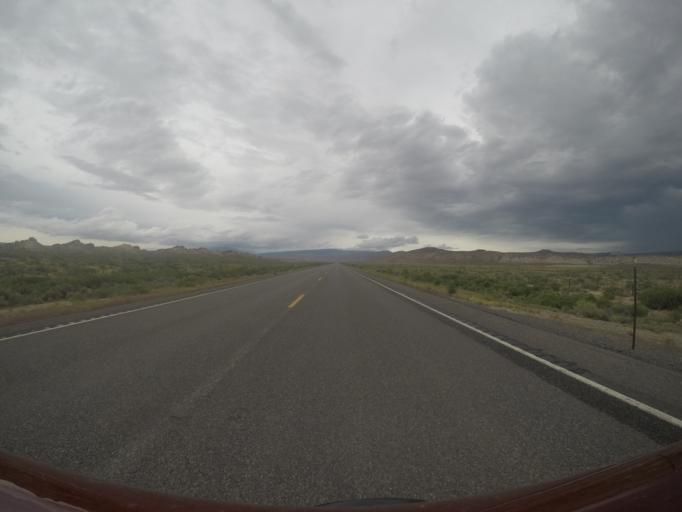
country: US
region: Wyoming
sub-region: Big Horn County
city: Lovell
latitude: 44.9042
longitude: -108.2906
